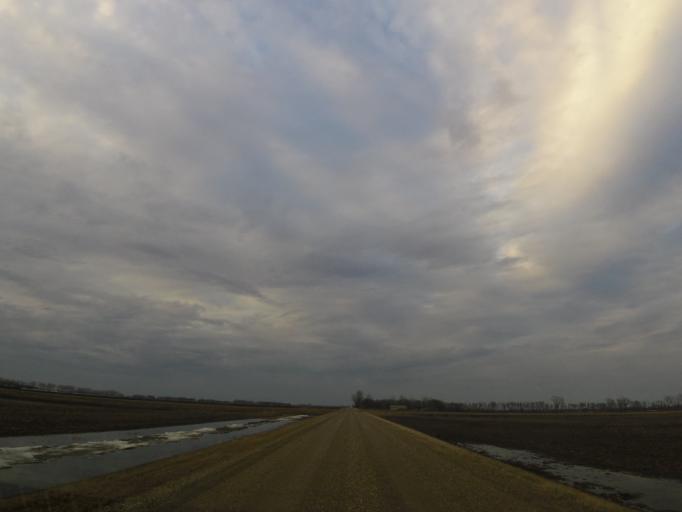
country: US
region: North Dakota
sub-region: Walsh County
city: Grafton
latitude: 48.3818
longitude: -97.2118
